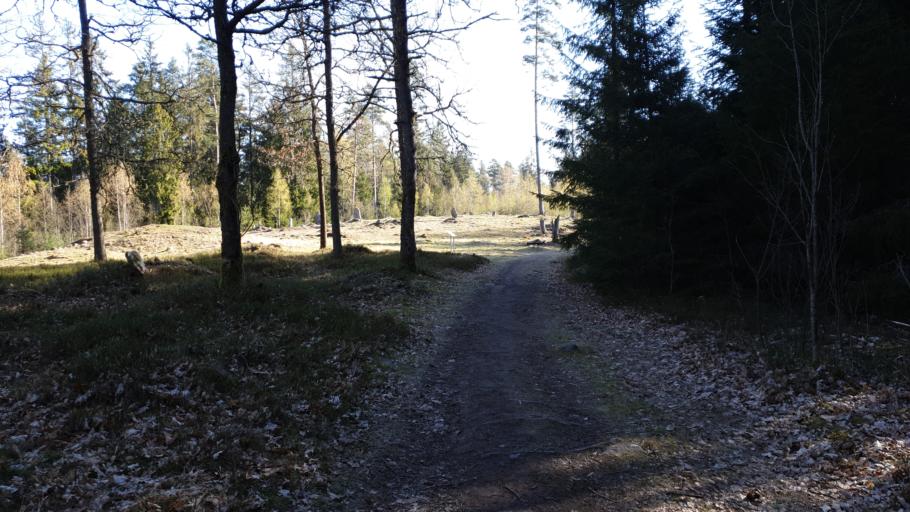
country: SE
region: Kronoberg
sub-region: Ljungby Kommun
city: Ljungby
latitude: 56.8349
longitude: 13.9067
